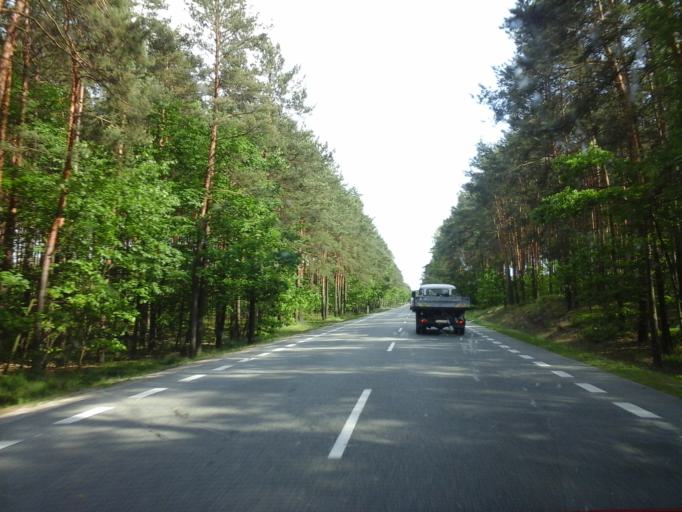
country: PL
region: Swietokrzyskie
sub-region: Powiat konecki
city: Ruda Maleniecka
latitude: 51.1581
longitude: 20.2312
